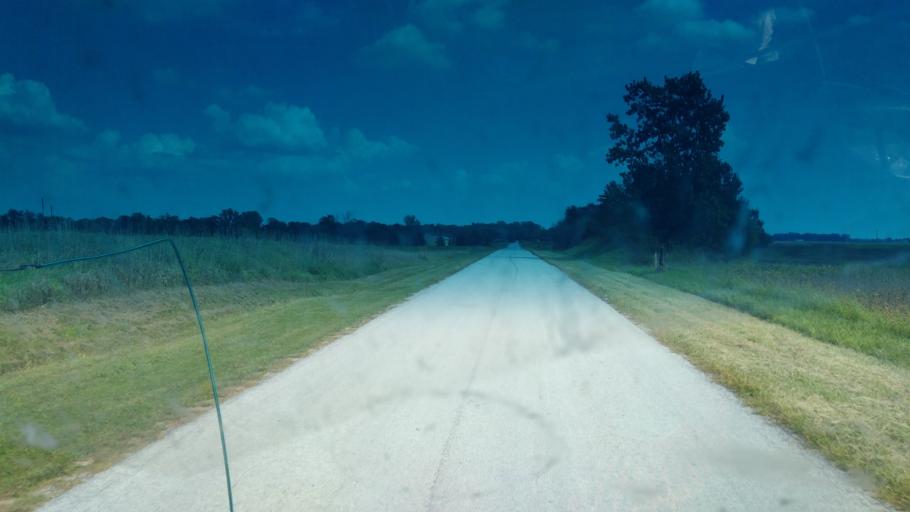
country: US
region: Ohio
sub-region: Hardin County
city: Kenton
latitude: 40.6605
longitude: -83.6813
